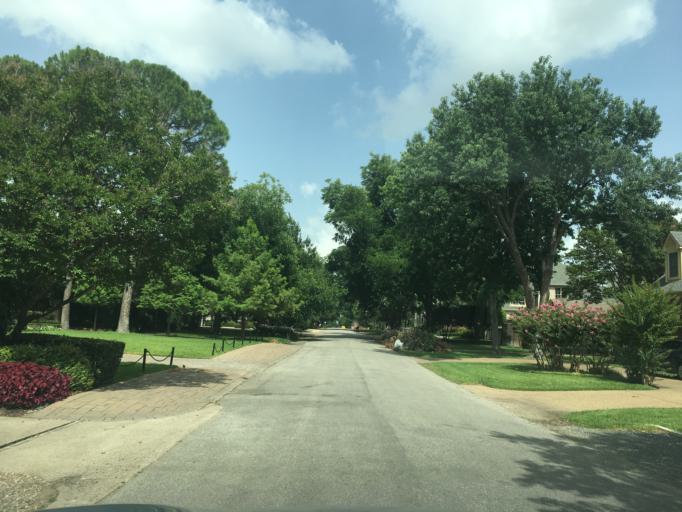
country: US
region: Texas
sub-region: Dallas County
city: University Park
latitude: 32.8843
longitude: -96.7955
